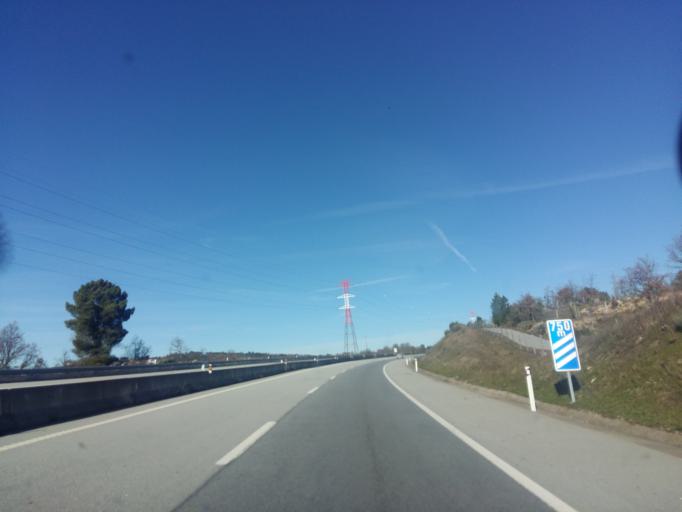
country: PT
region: Guarda
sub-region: Guarda
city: Sequeira
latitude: 40.5515
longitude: -7.2174
